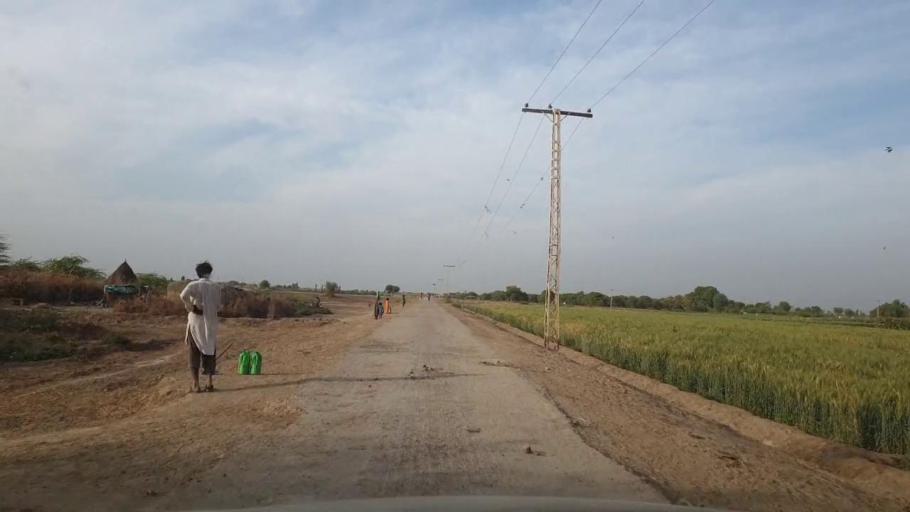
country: PK
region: Sindh
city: Kunri
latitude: 25.1987
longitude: 69.5199
